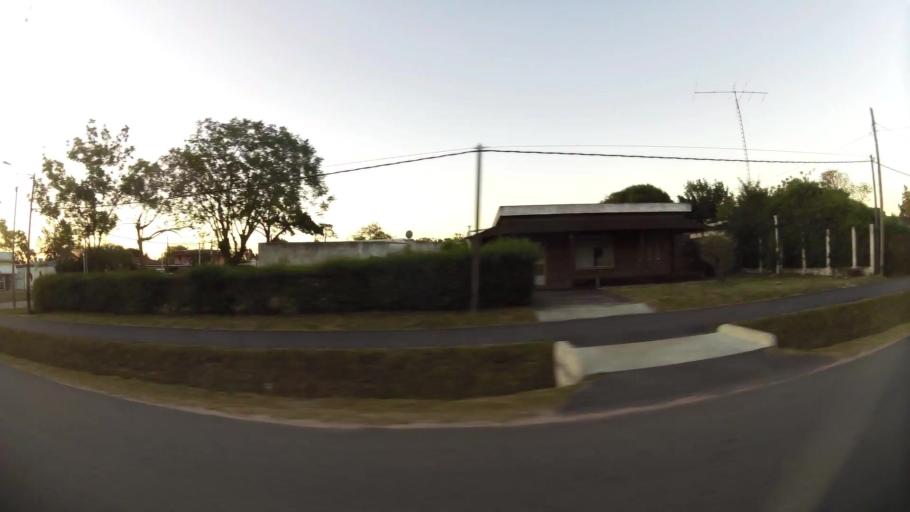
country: UY
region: Canelones
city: Barra de Carrasco
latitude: -34.8362
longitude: -55.9645
